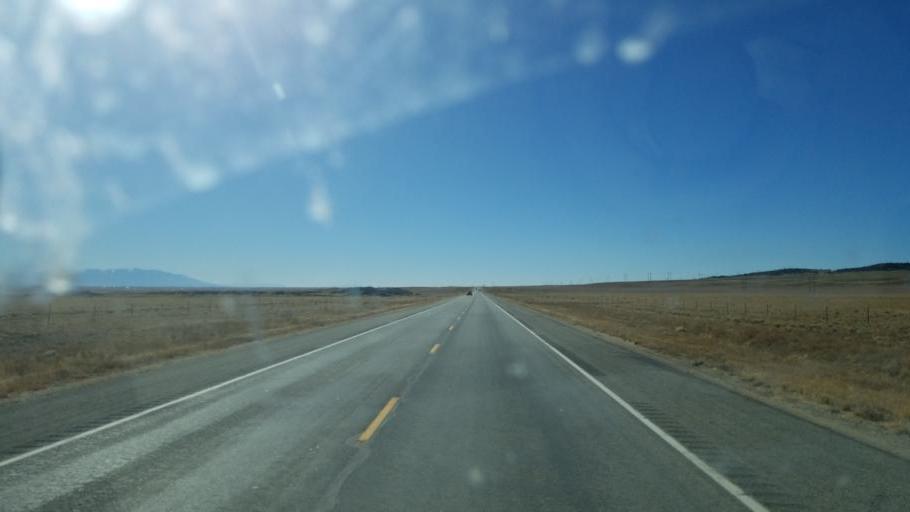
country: US
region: Colorado
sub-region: Saguache County
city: Saguache
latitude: 38.2092
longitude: -105.9427
